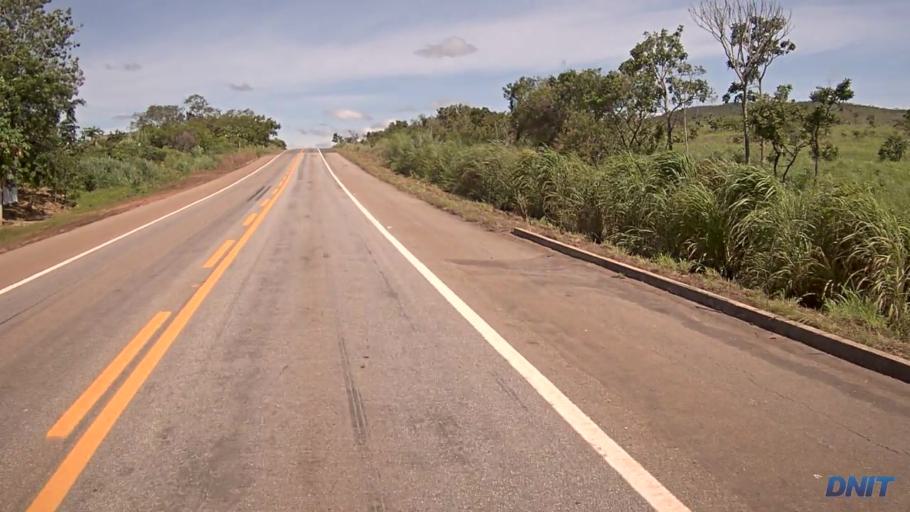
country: BR
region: Goias
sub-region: Barro Alto
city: Barro Alto
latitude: -15.1901
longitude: -48.7753
